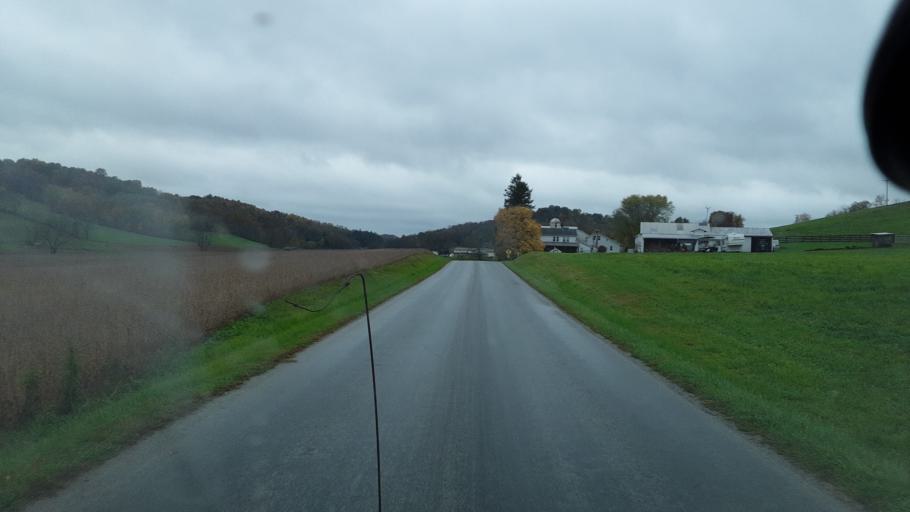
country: US
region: Ohio
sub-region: Coshocton County
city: West Lafayette
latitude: 40.3811
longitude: -81.7524
